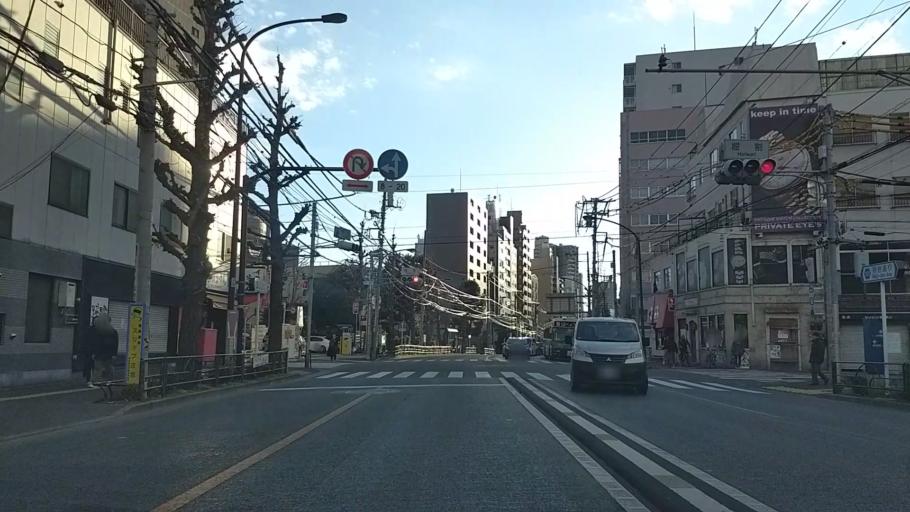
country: JP
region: Tokyo
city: Tokyo
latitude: 35.7426
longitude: 139.7266
